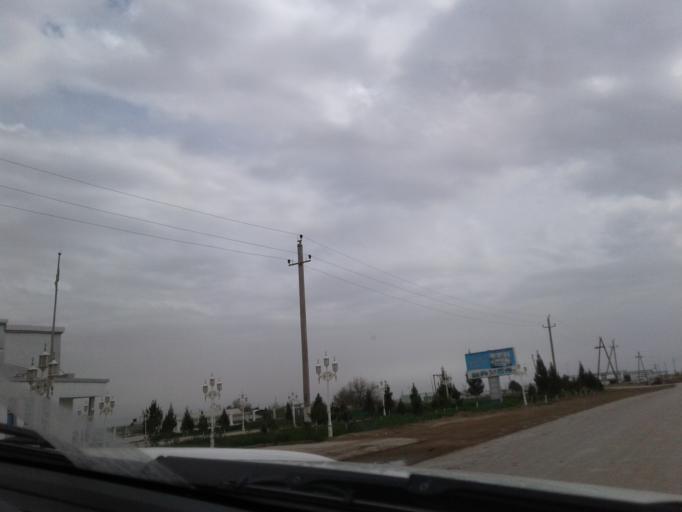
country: TM
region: Lebap
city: Atamyrat
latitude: 38.2199
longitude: 64.7263
